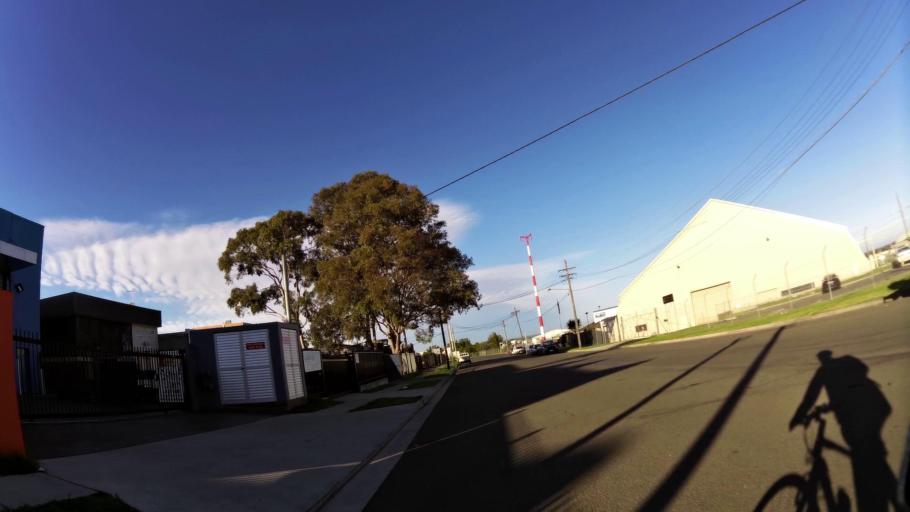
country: AU
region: New South Wales
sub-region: Bankstown
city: Milperra
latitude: -33.9181
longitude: 150.9979
